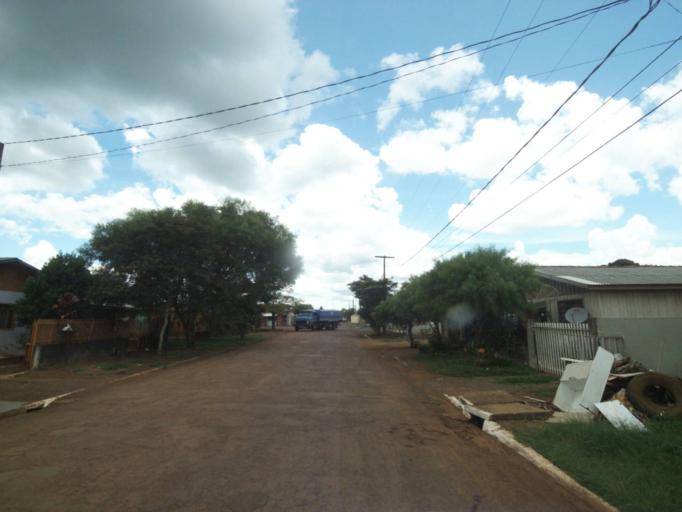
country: BR
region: Parana
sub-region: Guaraniacu
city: Guaraniacu
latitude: -25.1059
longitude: -52.8530
